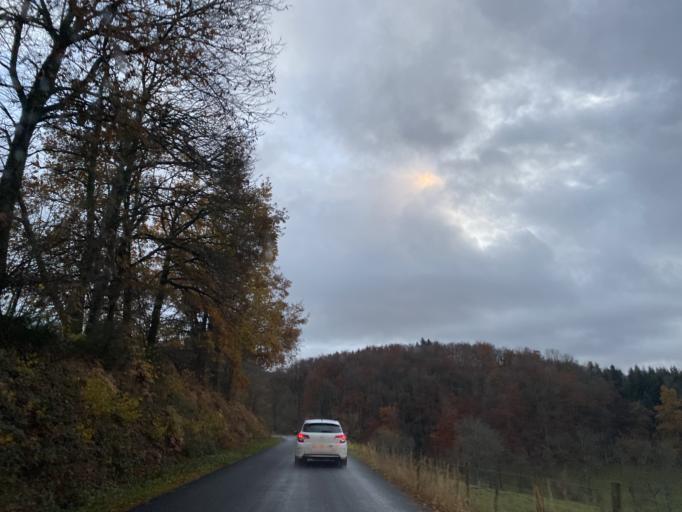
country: FR
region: Auvergne
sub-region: Departement du Puy-de-Dome
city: Cunlhat
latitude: 45.6094
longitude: 3.5692
